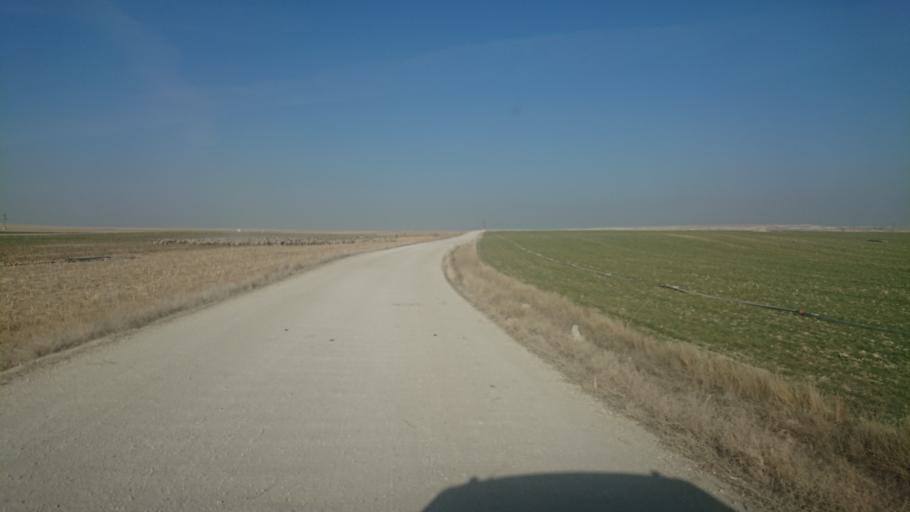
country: TR
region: Aksaray
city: Sultanhani
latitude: 38.0437
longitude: 33.6063
